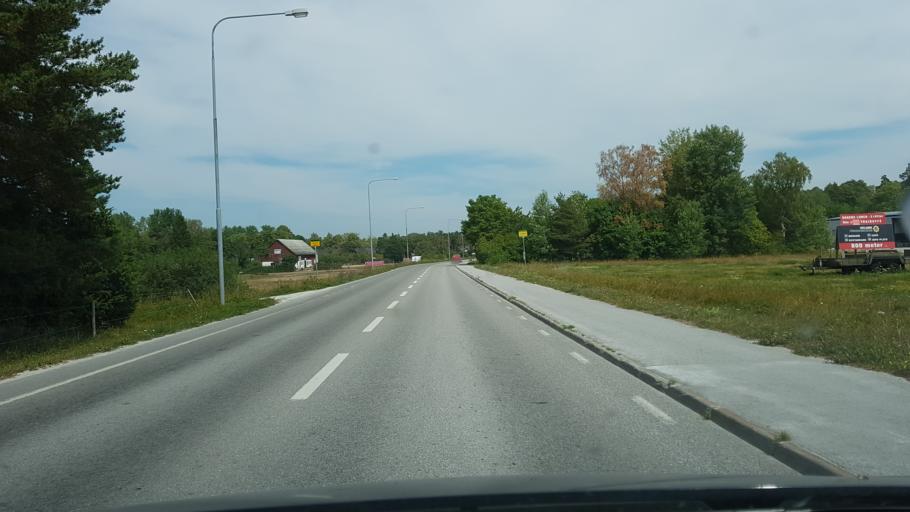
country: SE
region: Gotland
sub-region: Gotland
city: Slite
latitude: 57.7316
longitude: 18.5988
